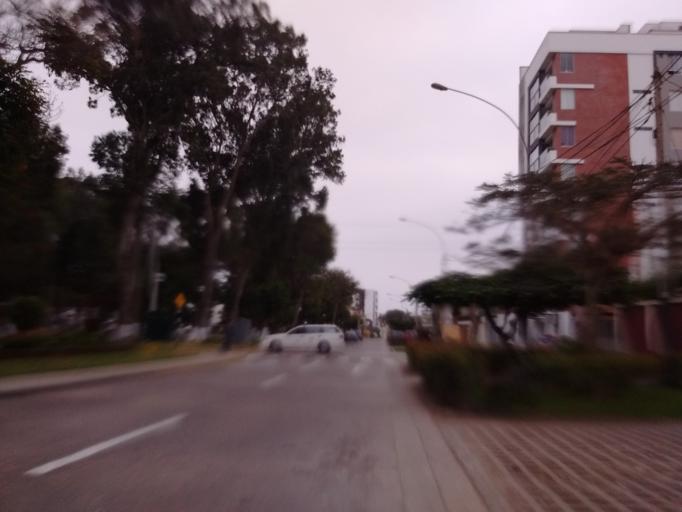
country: PE
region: Lima
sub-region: Lima
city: San Isidro
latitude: -12.0736
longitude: -77.0687
